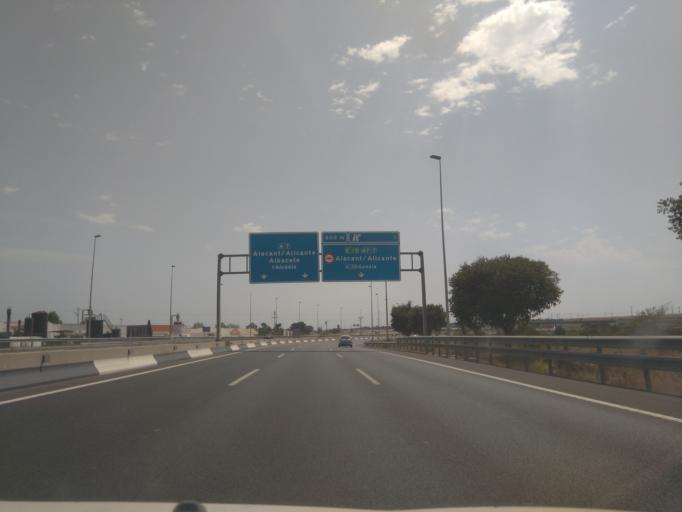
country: ES
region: Valencia
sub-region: Provincia de Valencia
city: Silla
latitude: 39.3550
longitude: -0.4258
